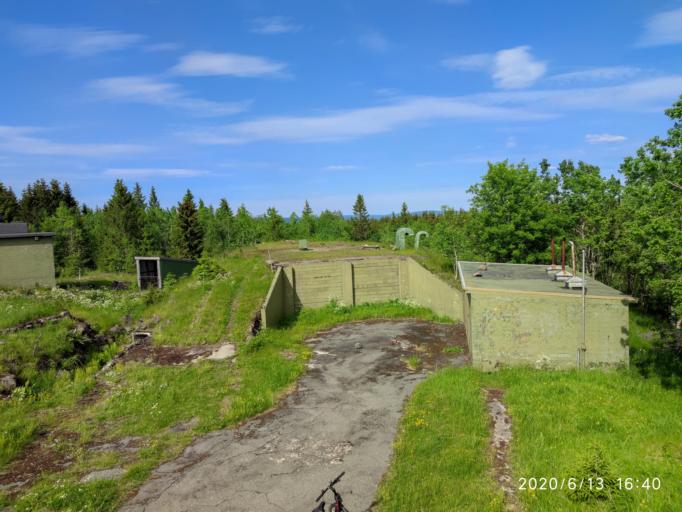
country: NO
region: Akershus
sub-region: Asker
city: Asker
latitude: 59.8568
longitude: 10.3790
